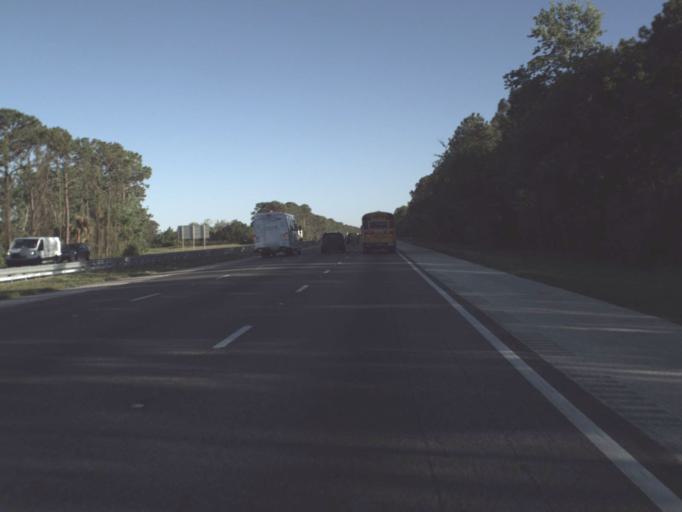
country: US
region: Florida
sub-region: Flagler County
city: Flagler Beach
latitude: 29.4515
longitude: -81.1746
